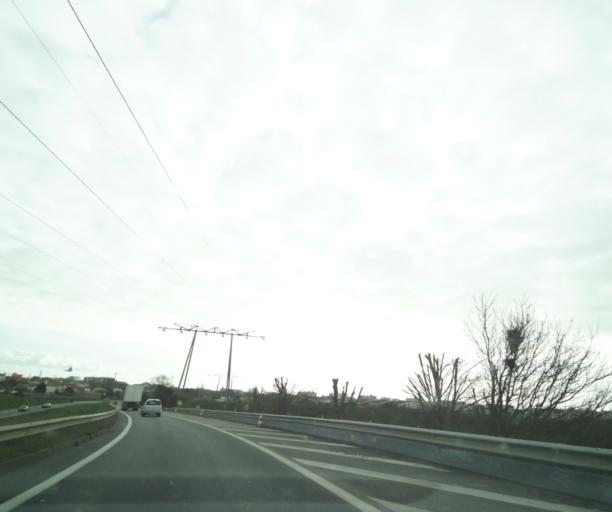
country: FR
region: Poitou-Charentes
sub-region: Departement de la Charente-Maritime
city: La Rochelle
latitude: 46.1708
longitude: -1.1902
